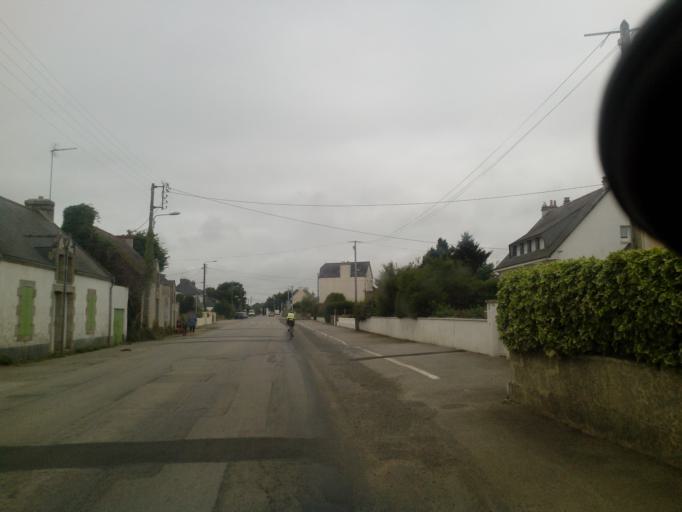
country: FR
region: Brittany
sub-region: Departement du Morbihan
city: Merlevenez
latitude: 47.6992
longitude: -3.2548
